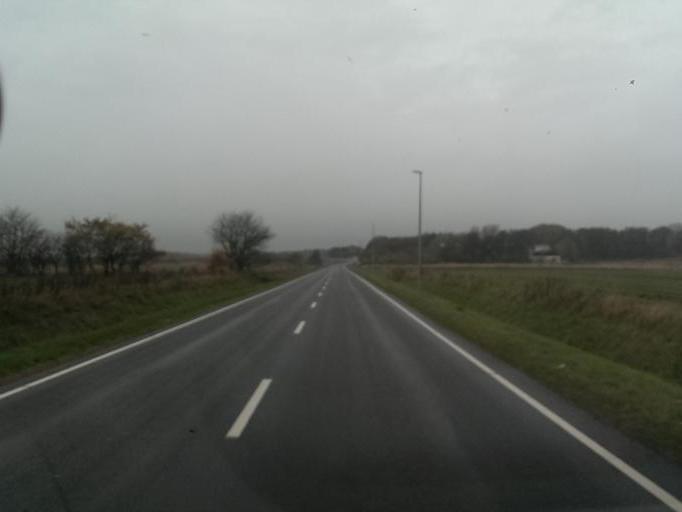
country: DK
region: South Denmark
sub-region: Esbjerg Kommune
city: Tjaereborg
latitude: 55.4601
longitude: 8.5678
